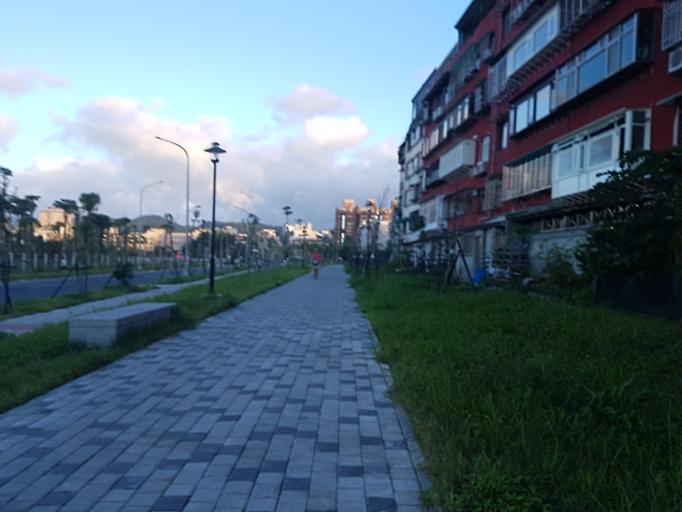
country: TW
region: Taipei
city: Taipei
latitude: 24.9770
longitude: 121.5279
